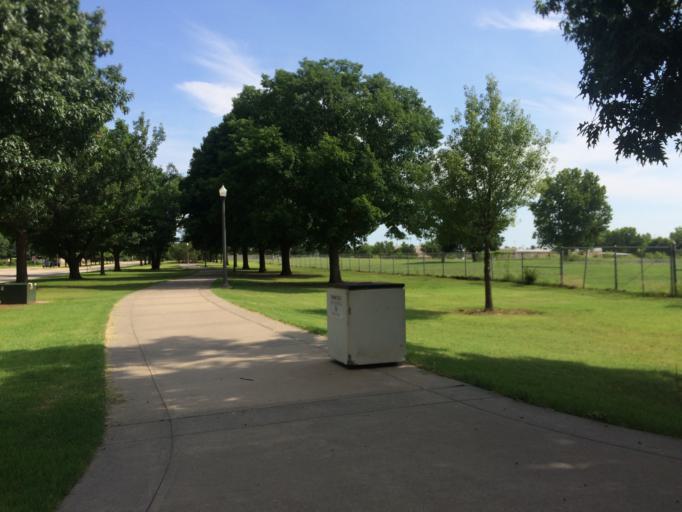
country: US
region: Oklahoma
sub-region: Cleveland County
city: Norman
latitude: 35.1825
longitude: -97.4498
